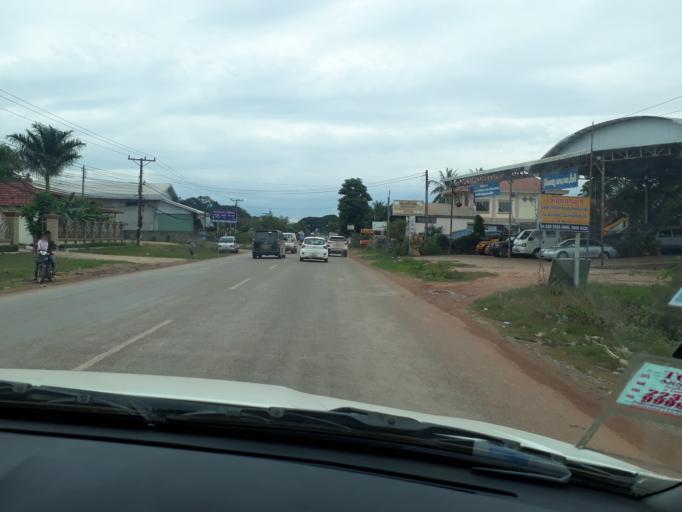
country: LA
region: Vientiane
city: Muang Phon-Hong
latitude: 18.3396
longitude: 102.4338
